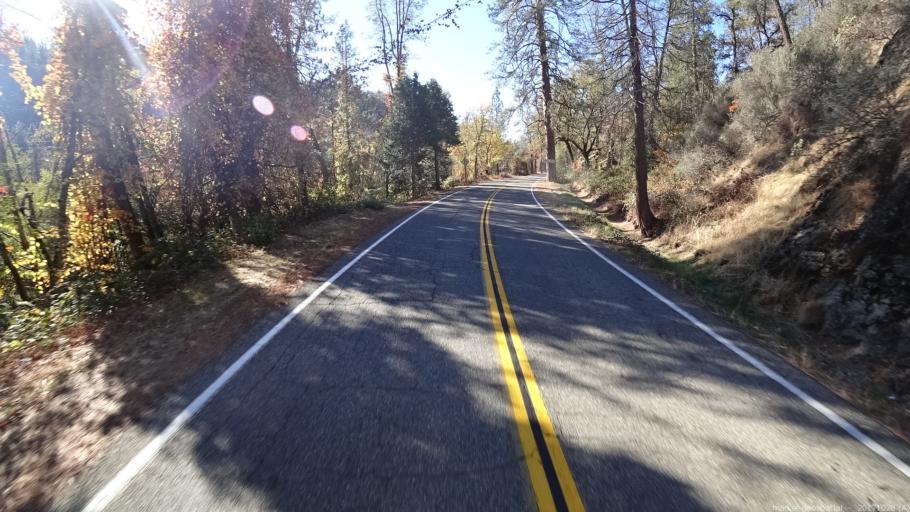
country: US
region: California
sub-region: Trinity County
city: Lewiston
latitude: 40.7522
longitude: -122.6170
